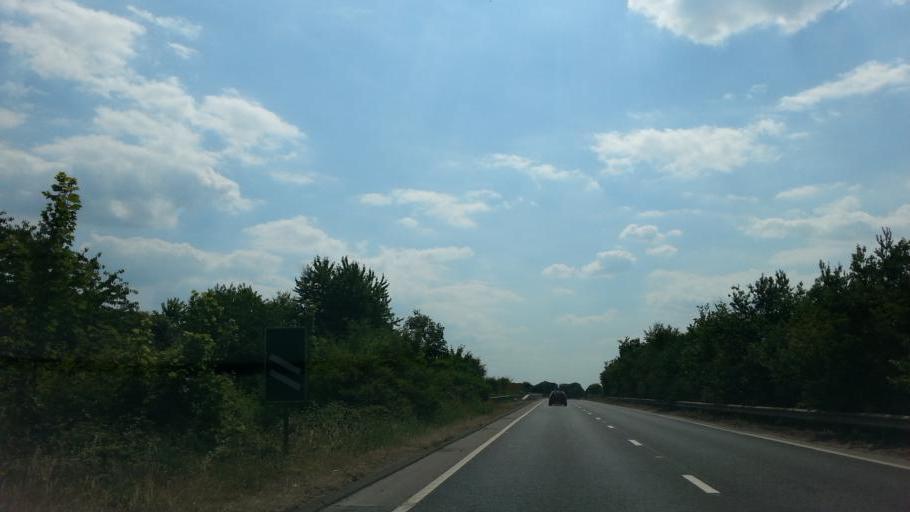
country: GB
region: England
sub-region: Suffolk
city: Newmarket
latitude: 52.2748
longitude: 0.4536
